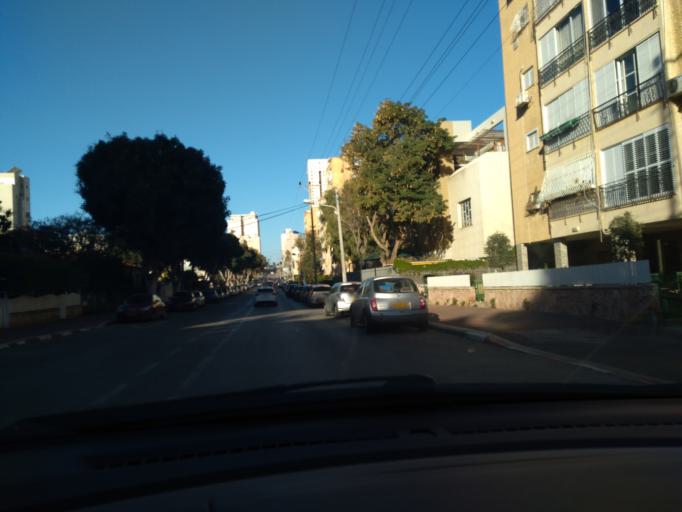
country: IL
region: Central District
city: Netanya
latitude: 32.3383
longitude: 34.8589
